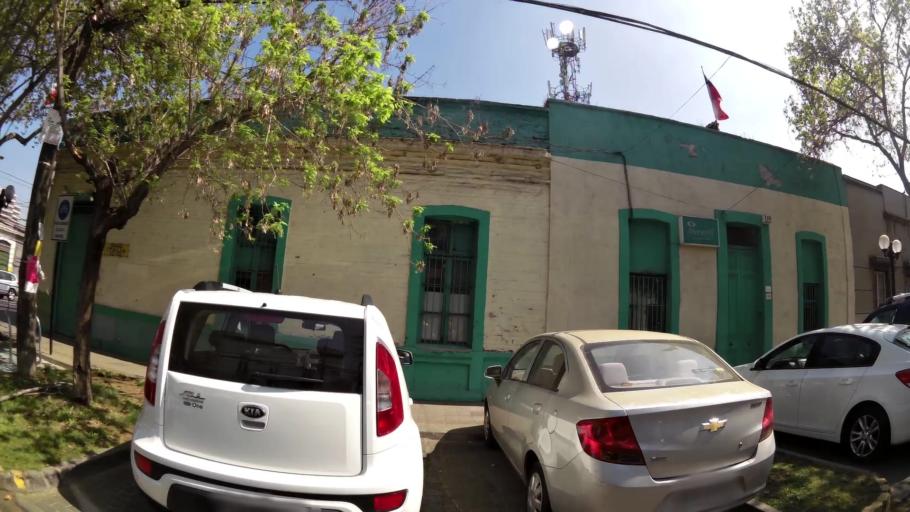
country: CL
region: Santiago Metropolitan
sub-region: Provincia de Santiago
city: Santiago
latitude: -33.4460
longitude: -70.6253
